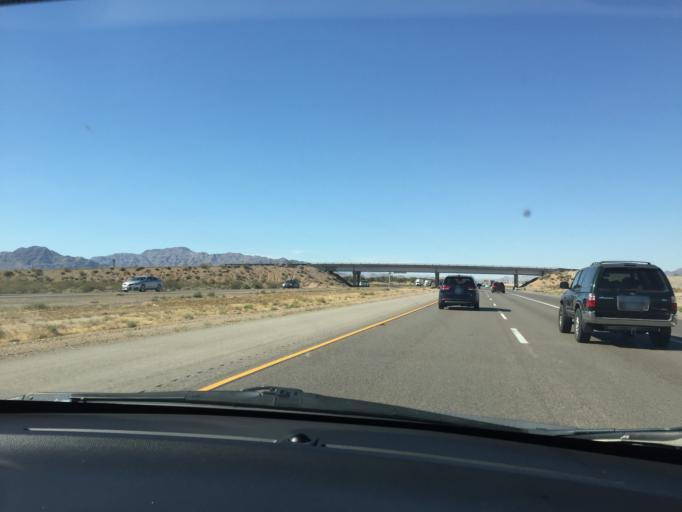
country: US
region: Nevada
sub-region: Clark County
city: Sandy Valley
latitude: 35.5388
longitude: -115.4205
